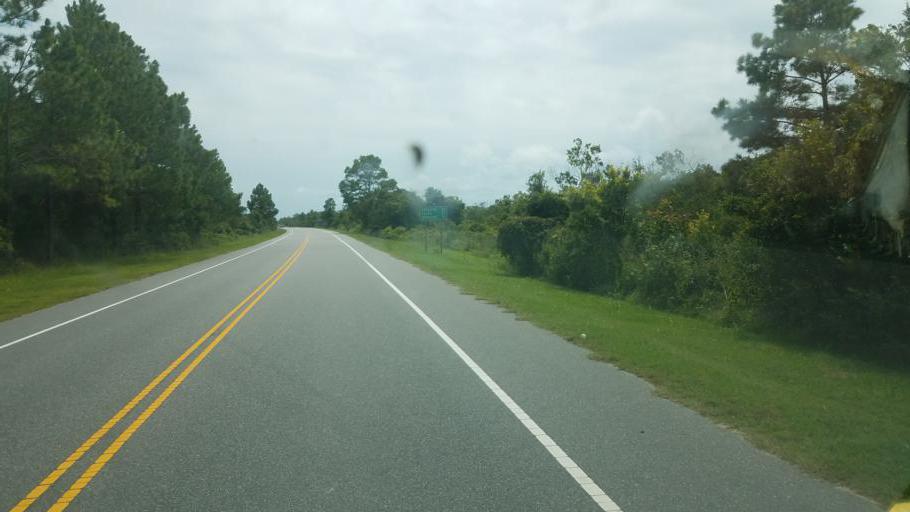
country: US
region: North Carolina
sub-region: Dare County
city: Nags Head
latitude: 35.9001
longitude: -75.5962
